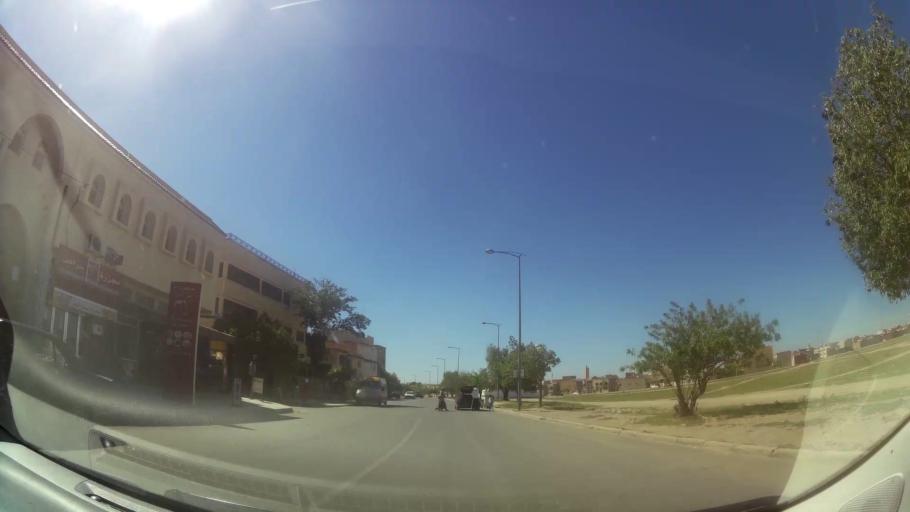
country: MA
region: Oriental
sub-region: Oujda-Angad
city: Oujda
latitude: 34.6654
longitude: -1.8689
